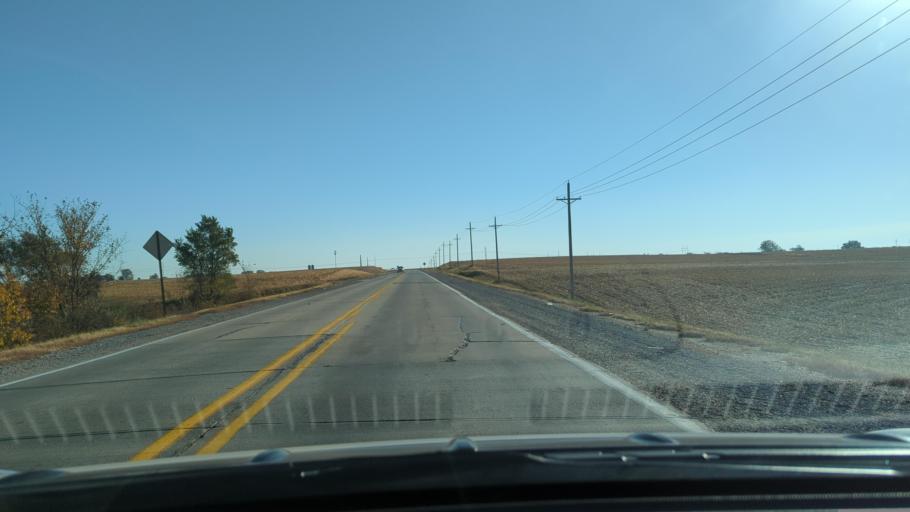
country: US
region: Nebraska
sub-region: Sarpy County
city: Offutt Air Force Base
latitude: 41.0927
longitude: -95.9851
